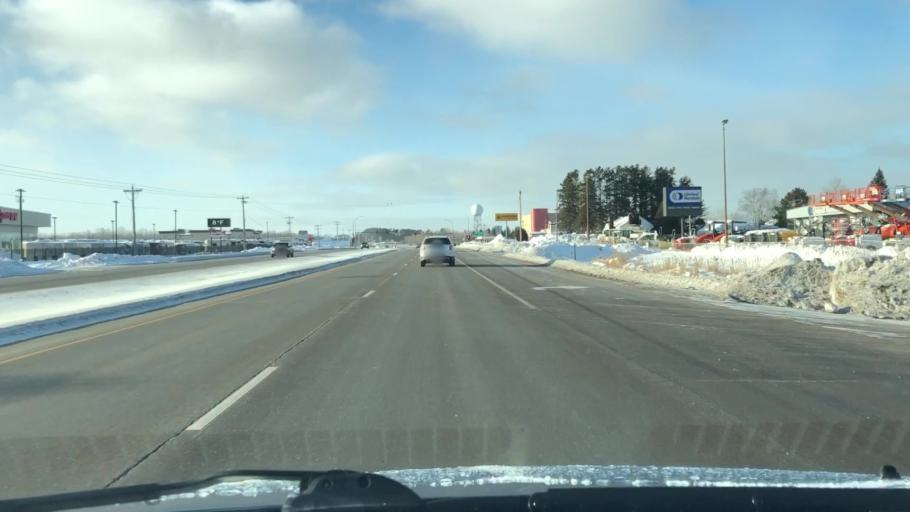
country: US
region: Minnesota
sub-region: Saint Louis County
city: Hermantown
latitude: 46.8316
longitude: -92.2020
